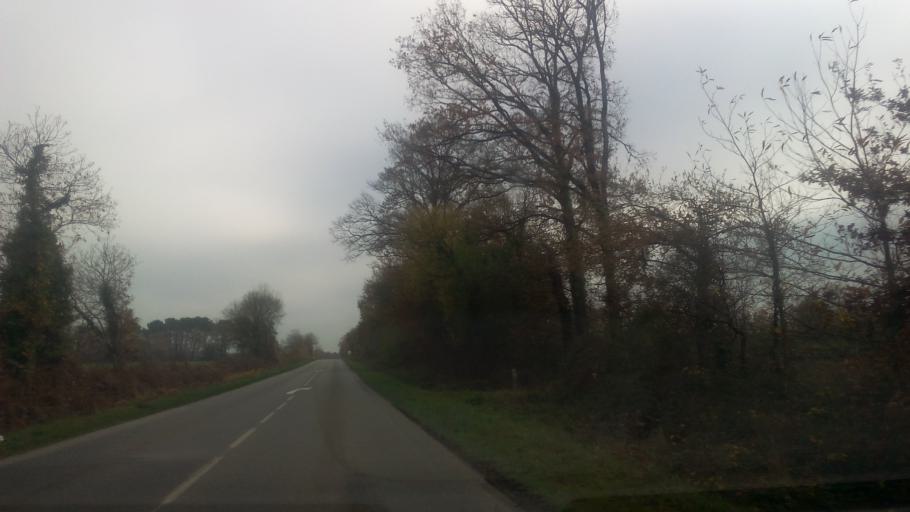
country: FR
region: Brittany
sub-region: Departement du Morbihan
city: Peillac
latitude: 47.7144
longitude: -2.1995
